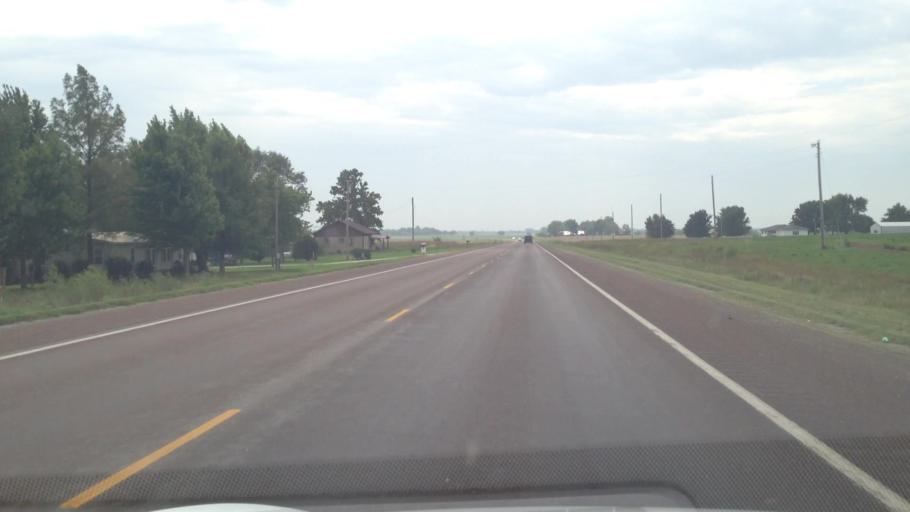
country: US
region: Kansas
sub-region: Crawford County
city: Girard
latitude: 37.4930
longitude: -94.8426
